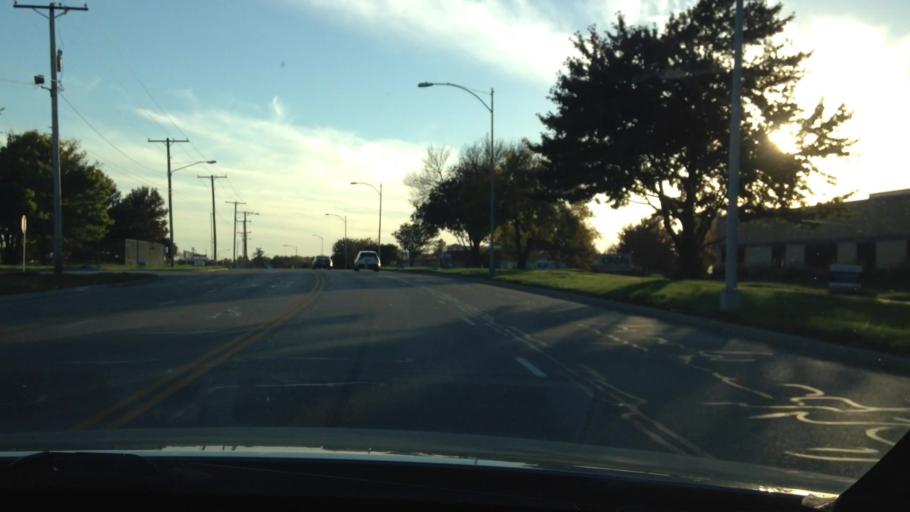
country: US
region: Kansas
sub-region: Johnson County
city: Olathe
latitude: 38.9054
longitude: -94.7830
